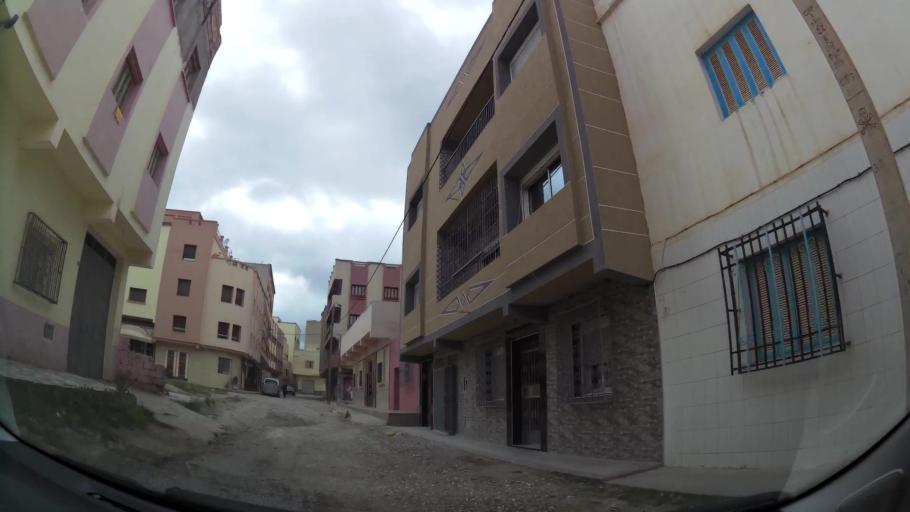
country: MA
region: Oriental
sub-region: Nador
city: Nador
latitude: 35.1688
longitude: -2.9400
